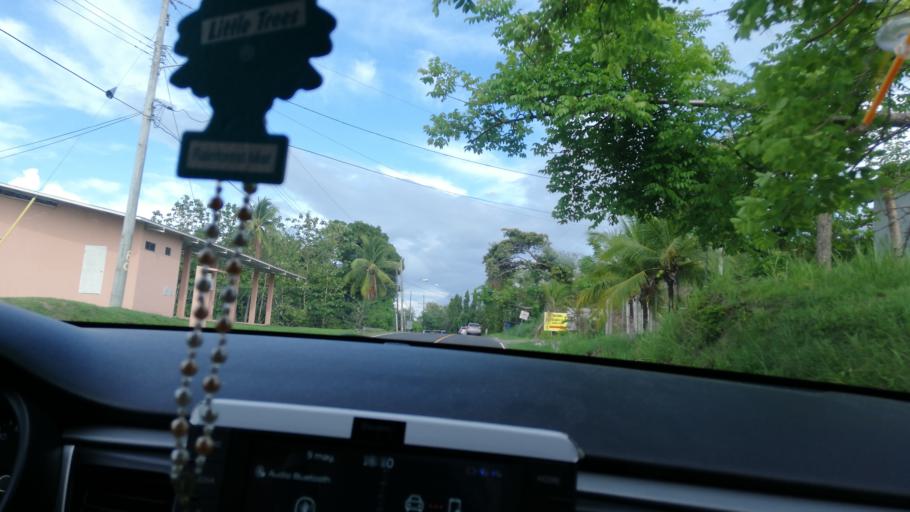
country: PA
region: Panama
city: Las Colinas
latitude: 8.4853
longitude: -80.0200
